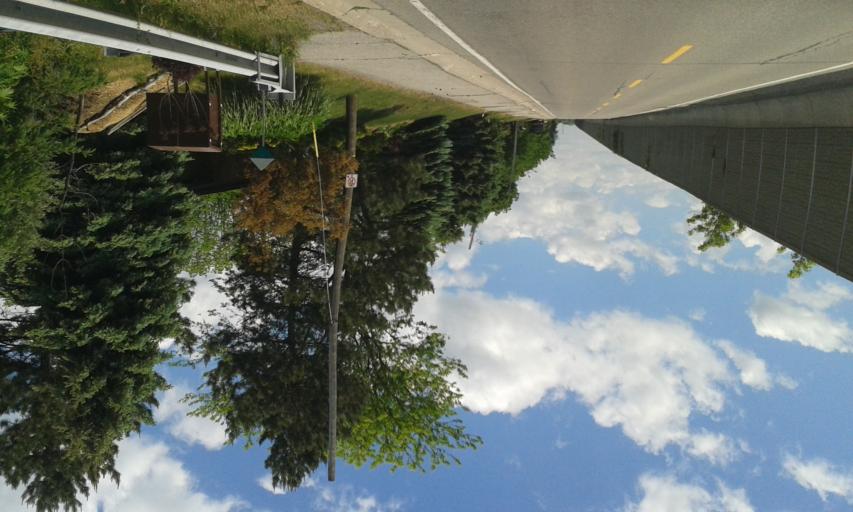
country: CA
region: Ontario
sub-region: Regional Municipality of Niagara
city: St. Catharines
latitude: 43.1803
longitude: -79.3282
